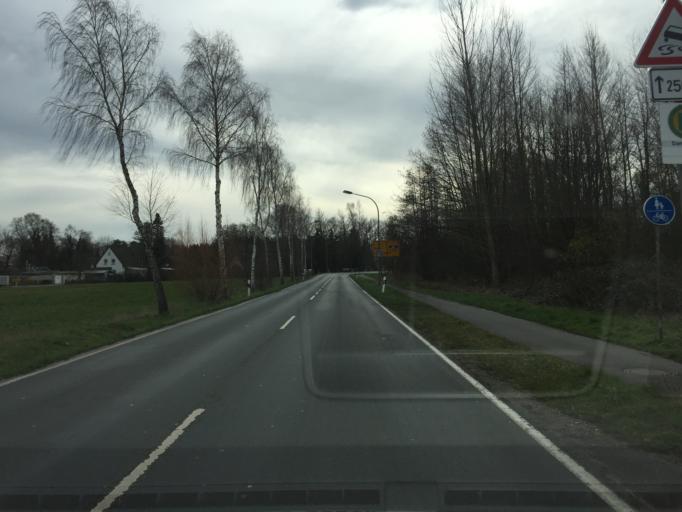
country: DE
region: North Rhine-Westphalia
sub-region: Regierungsbezirk Detmold
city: Lage
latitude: 51.9576
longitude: 8.8118
